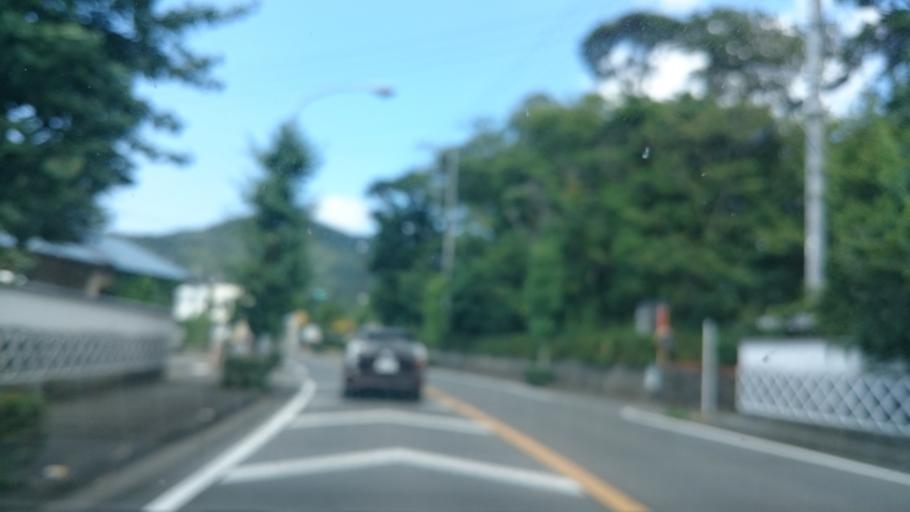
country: JP
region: Shizuoka
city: Shimoda
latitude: 34.7517
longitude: 138.7819
